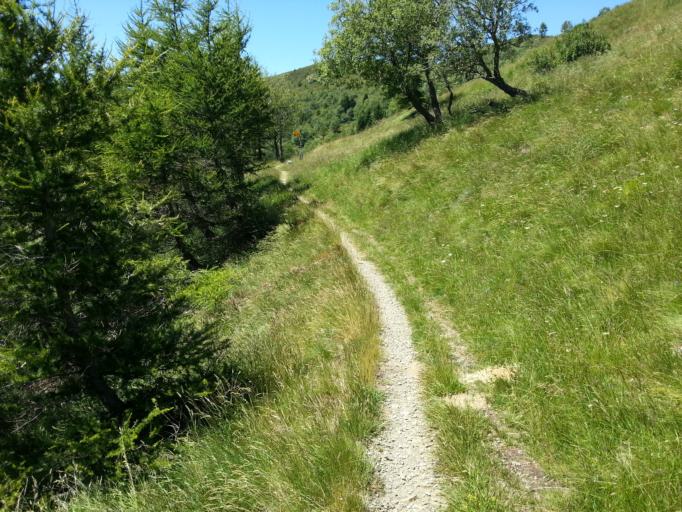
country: CH
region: Ticino
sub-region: Bellinzona District
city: Camorino
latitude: 46.1086
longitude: 9.0342
